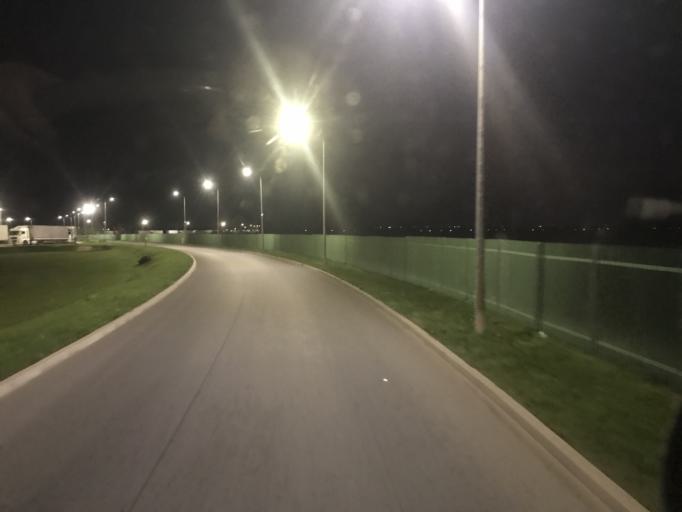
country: PL
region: Lublin Voivodeship
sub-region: Powiat bialski
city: Terespol
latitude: 52.0766
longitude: 23.5210
